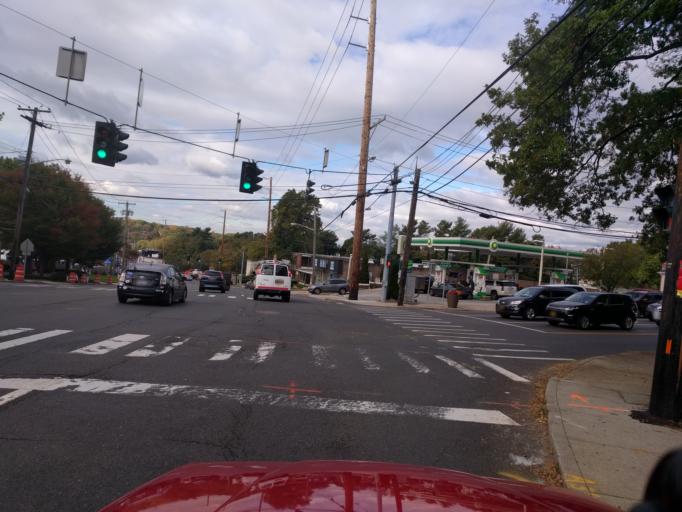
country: US
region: New York
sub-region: Nassau County
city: Manhasset
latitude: 40.7929
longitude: -73.6974
